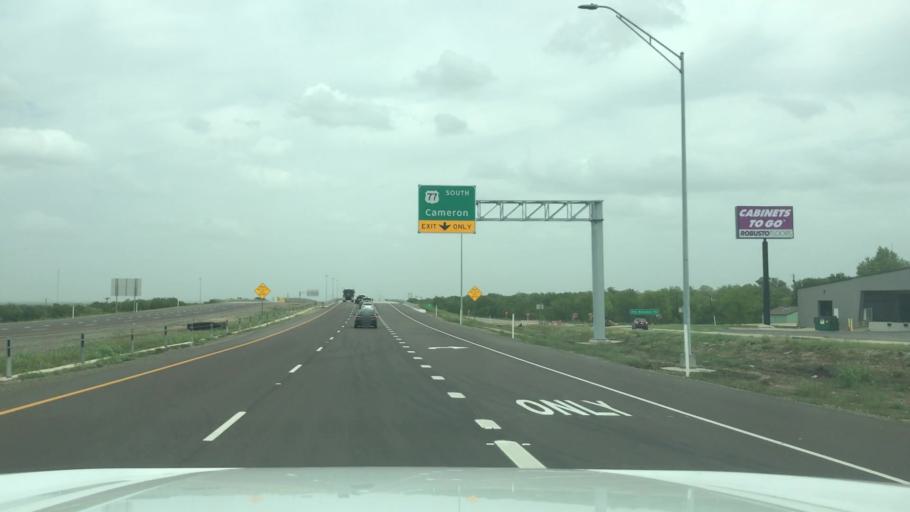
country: US
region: Texas
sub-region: McLennan County
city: Beverly
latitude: 31.4935
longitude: -97.1358
